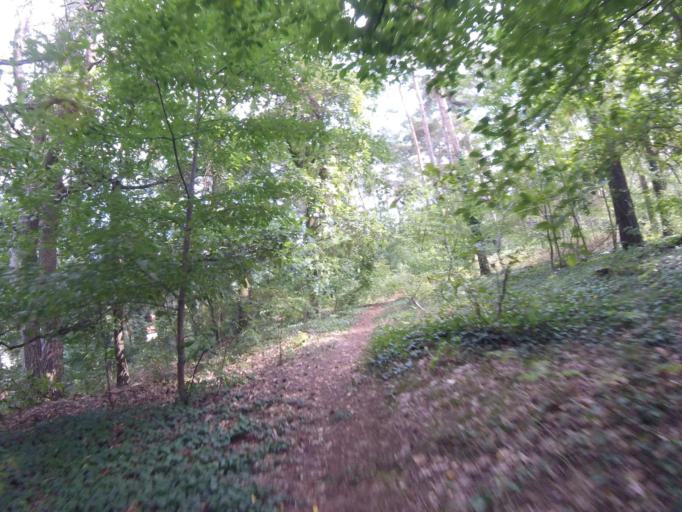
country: DE
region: Brandenburg
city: Konigs Wusterhausen
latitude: 52.2851
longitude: 13.6663
